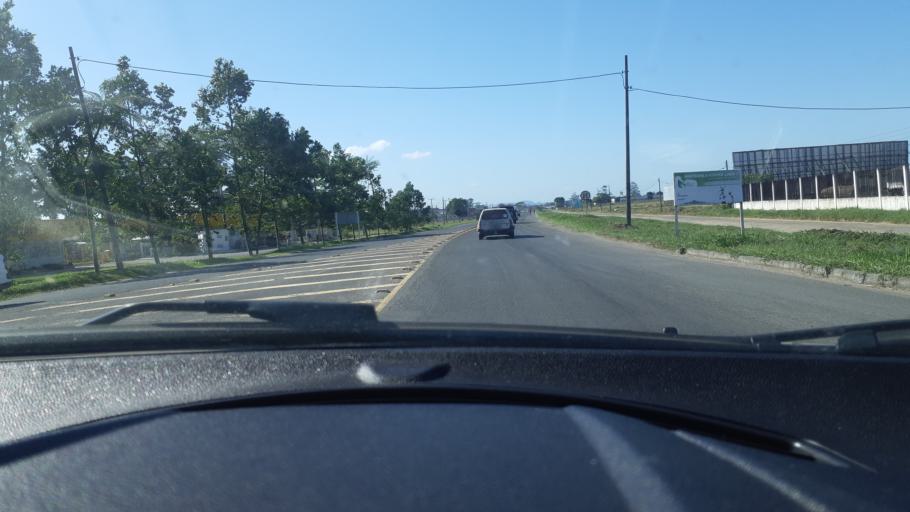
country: BR
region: Santa Catarina
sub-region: Ararangua
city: Ararangua
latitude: -28.9631
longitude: -49.5192
